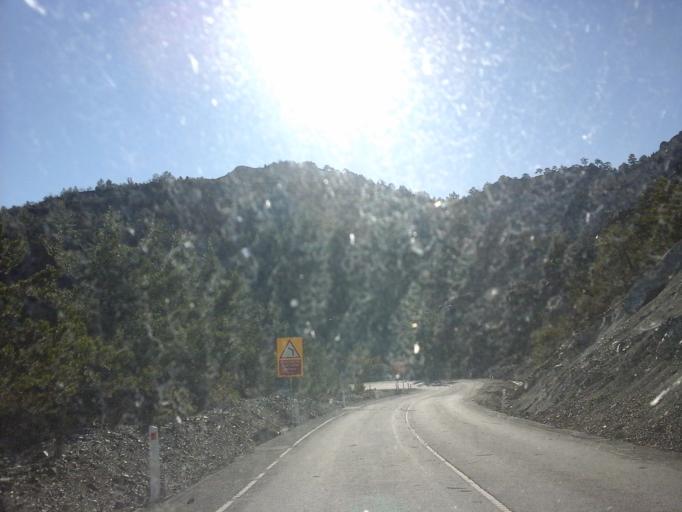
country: CY
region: Lefkosia
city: Kakopetria
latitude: 34.9309
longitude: 32.9155
